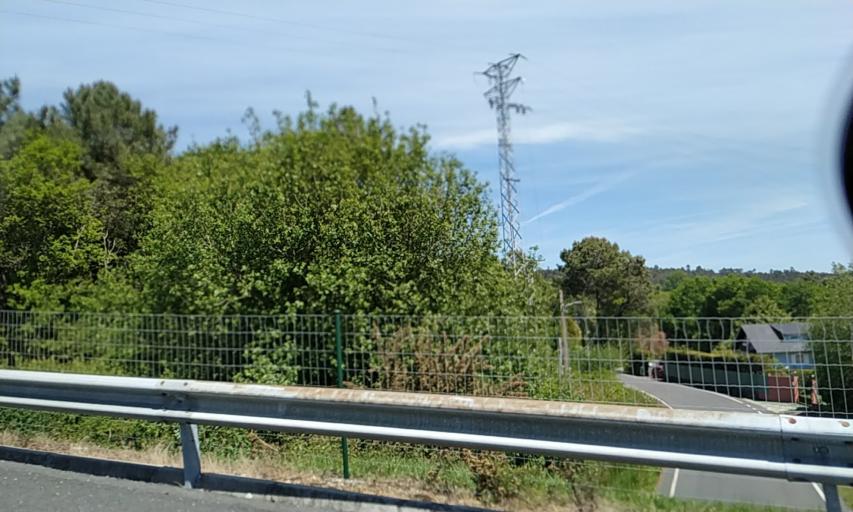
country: ES
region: Galicia
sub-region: Provincia da Coruna
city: Santiago de Compostela
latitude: 42.8266
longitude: -8.5713
